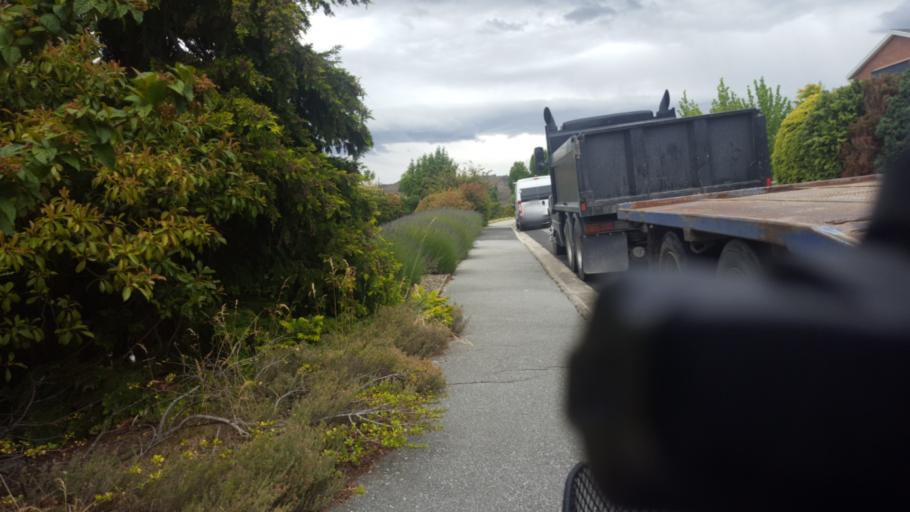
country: NZ
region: Otago
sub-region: Queenstown-Lakes District
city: Wanaka
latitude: -45.2626
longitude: 169.3805
